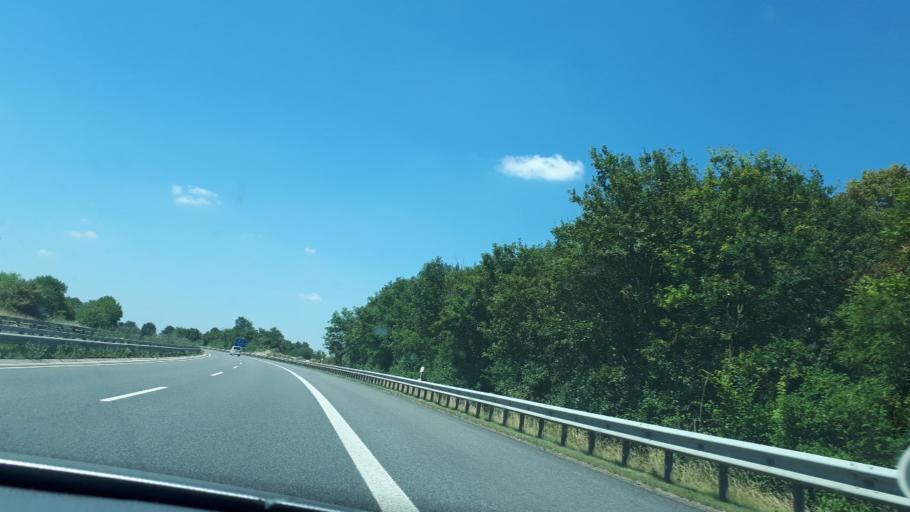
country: DE
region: Rheinland-Pfalz
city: Lonnig
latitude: 50.3420
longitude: 7.4292
